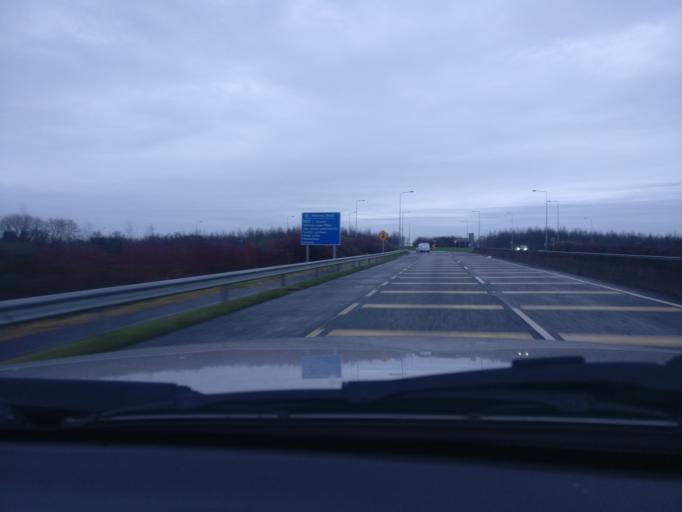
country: IE
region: Leinster
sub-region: An Mhi
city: Navan
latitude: 53.6407
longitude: -6.7376
